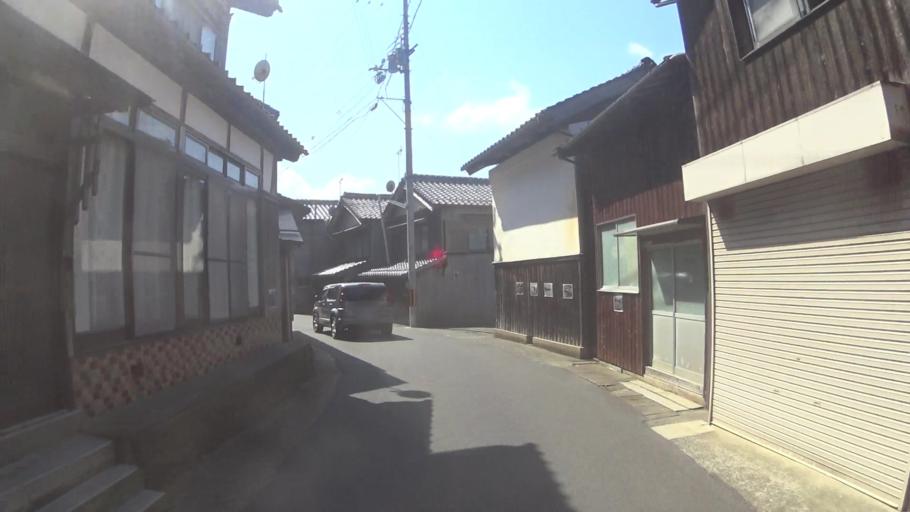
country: JP
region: Kyoto
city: Miyazu
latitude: 35.6692
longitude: 135.2928
